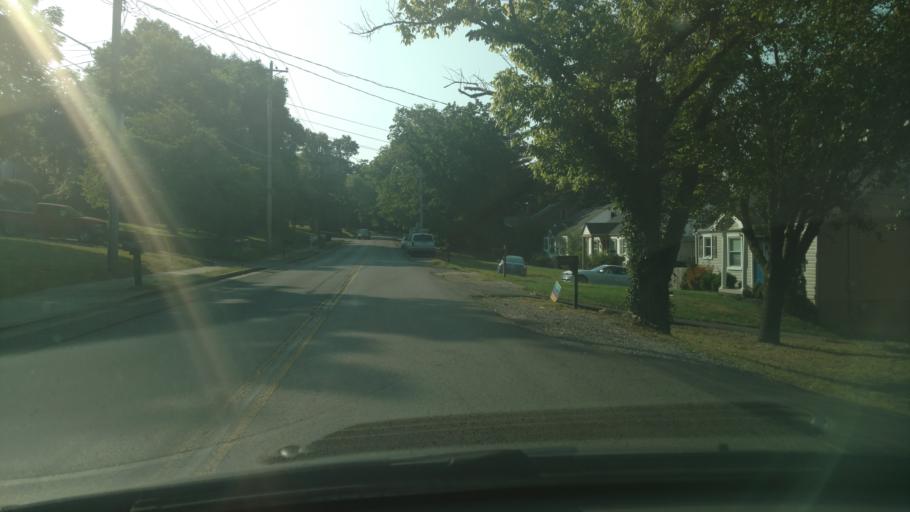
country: US
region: Tennessee
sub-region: Davidson County
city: Nashville
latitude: 36.2148
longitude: -86.7183
